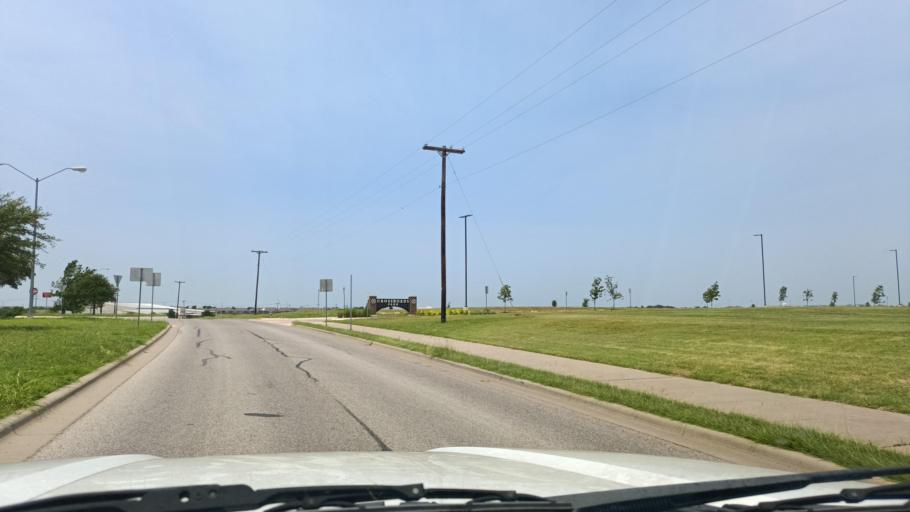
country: US
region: Texas
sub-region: Bell County
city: Morgans Point Resort
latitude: 31.1273
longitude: -97.4090
